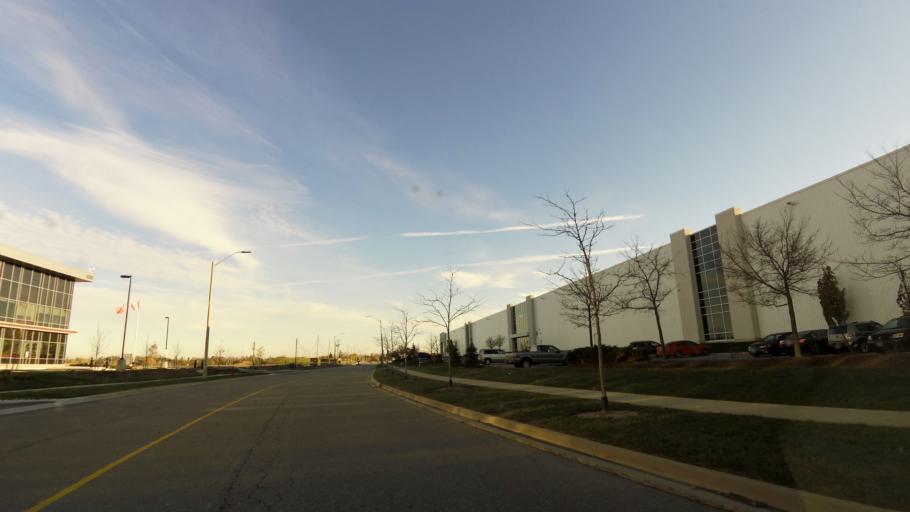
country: CA
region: Ontario
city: Mississauga
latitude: 43.5882
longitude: -79.7323
